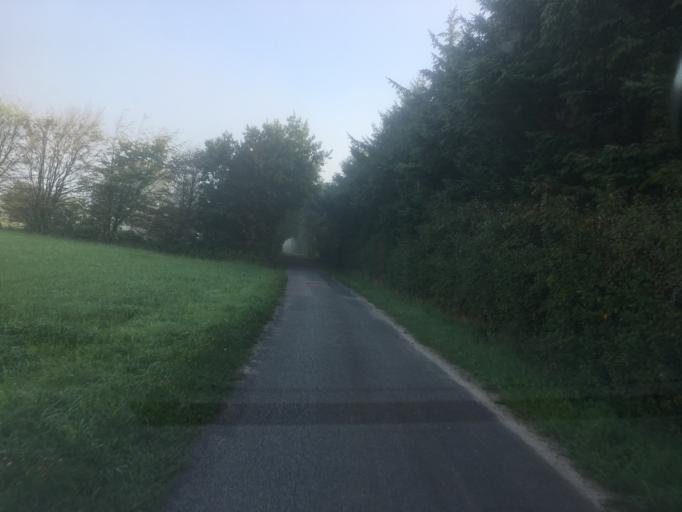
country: DK
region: South Denmark
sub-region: Tonder Kommune
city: Logumkloster
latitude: 55.0141
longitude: 8.9144
